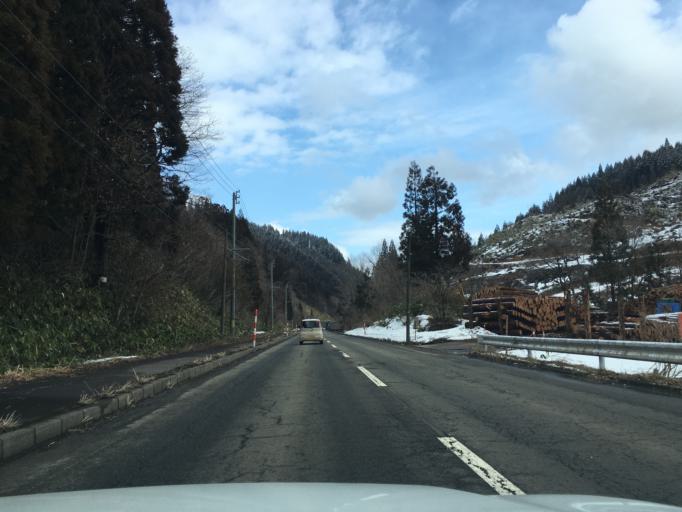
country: JP
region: Akita
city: Takanosu
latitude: 39.9921
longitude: 140.2479
